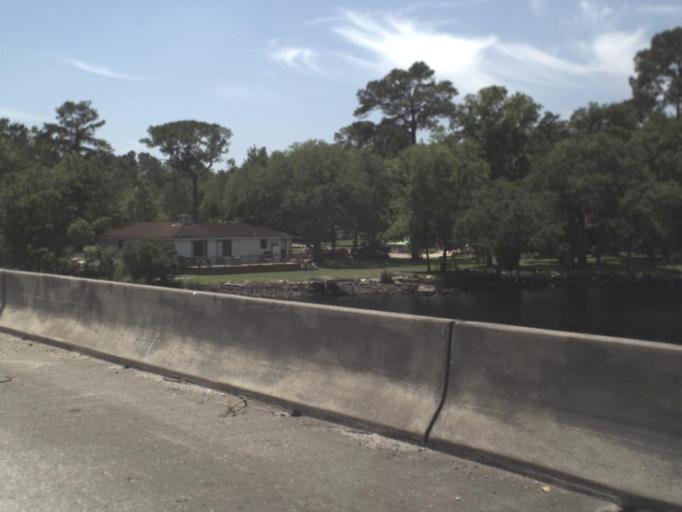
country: US
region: Florida
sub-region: Nassau County
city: Nassau Village-Ratliff
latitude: 30.4219
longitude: -81.7350
